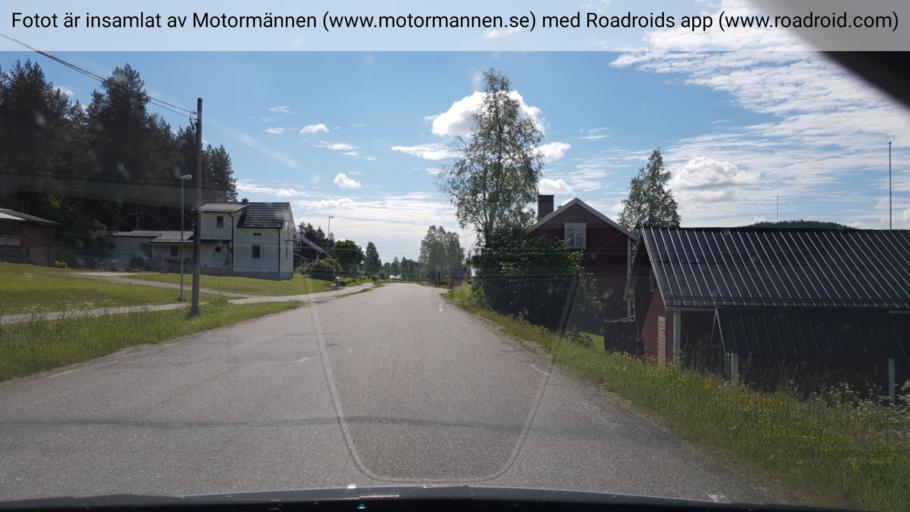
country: FI
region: Lapland
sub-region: Torniolaakso
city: Pello
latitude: 66.6663
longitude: 23.8431
